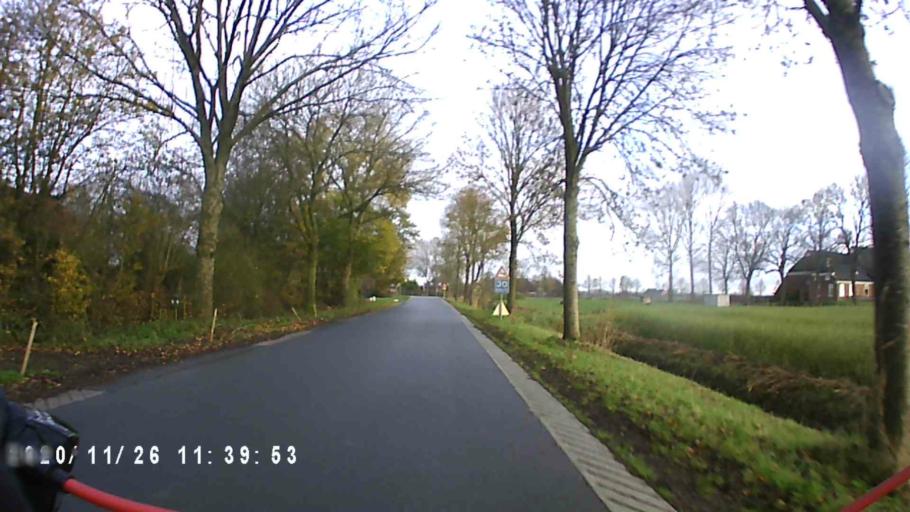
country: NL
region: Groningen
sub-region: Gemeente Bedum
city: Bedum
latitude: 53.2860
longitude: 6.5700
